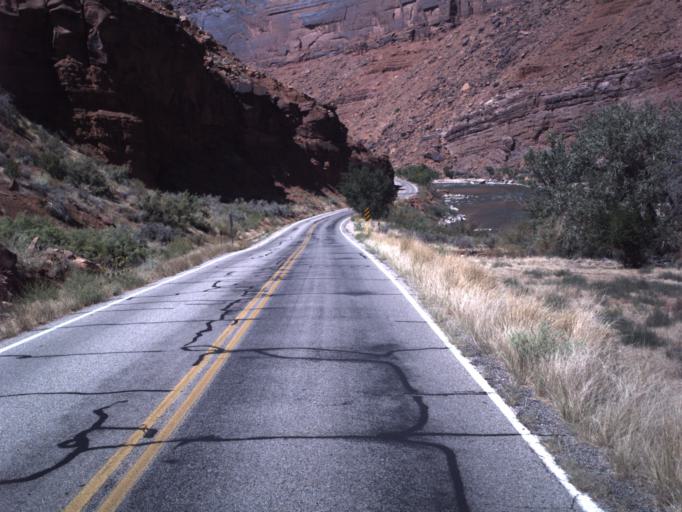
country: US
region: Utah
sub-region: Grand County
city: Moab
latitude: 38.6810
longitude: -109.4540
